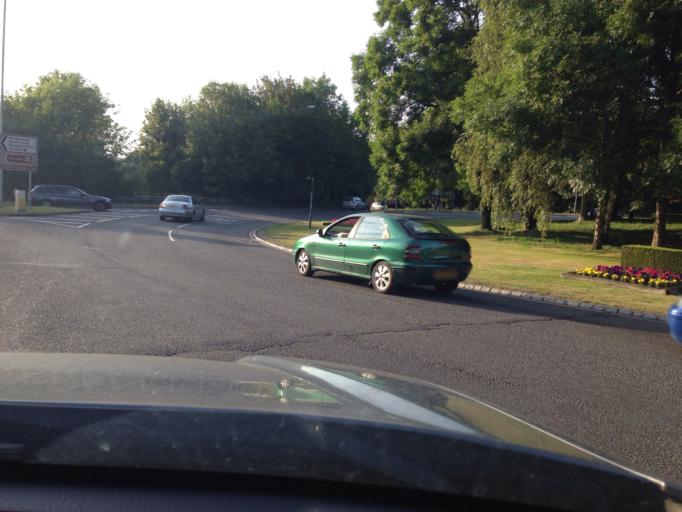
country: GB
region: England
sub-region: Buckinghamshire
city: Bourne End
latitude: 51.6056
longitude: -0.6936
